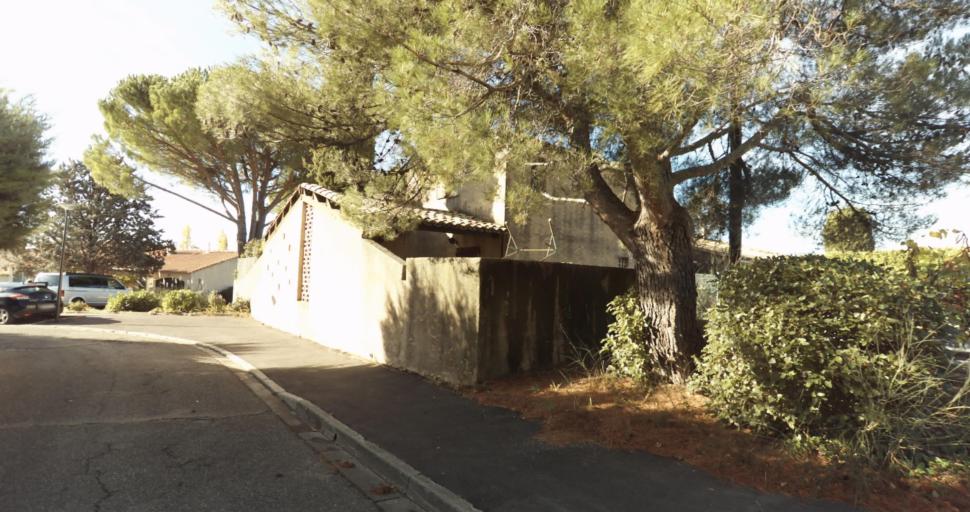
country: FR
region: Provence-Alpes-Cote d'Azur
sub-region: Departement des Bouches-du-Rhone
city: Venelles
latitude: 43.5910
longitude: 5.4706
